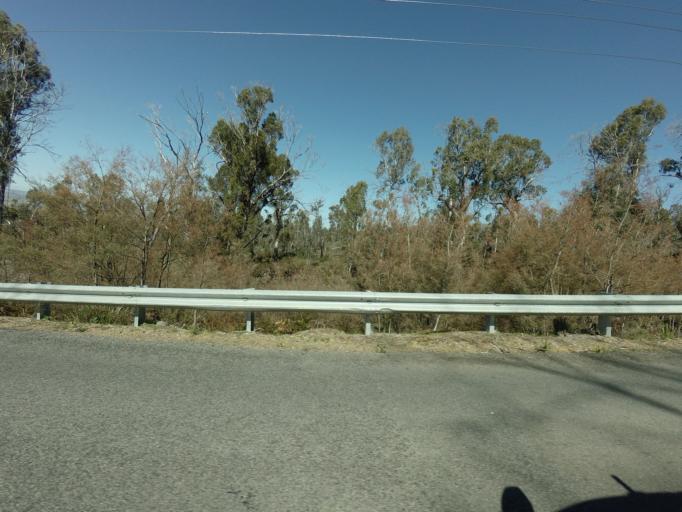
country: AU
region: Tasmania
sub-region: Derwent Valley
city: New Norfolk
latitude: -42.5460
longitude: 146.7145
